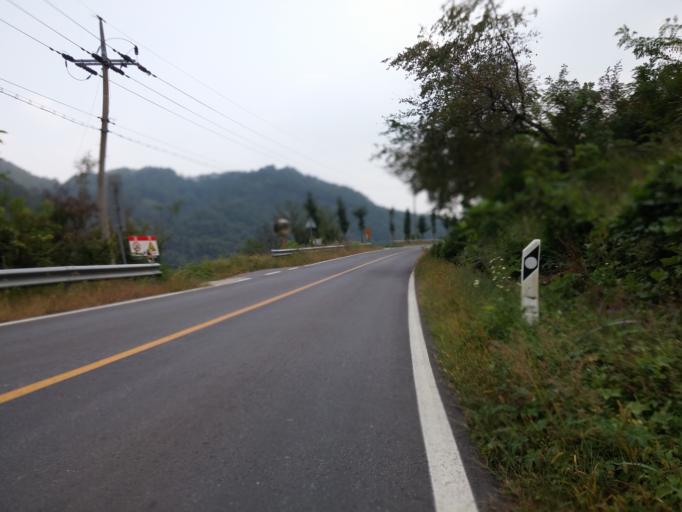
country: KR
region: Chungcheongbuk-do
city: Yong-dong
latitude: 36.3960
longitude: 127.8114
